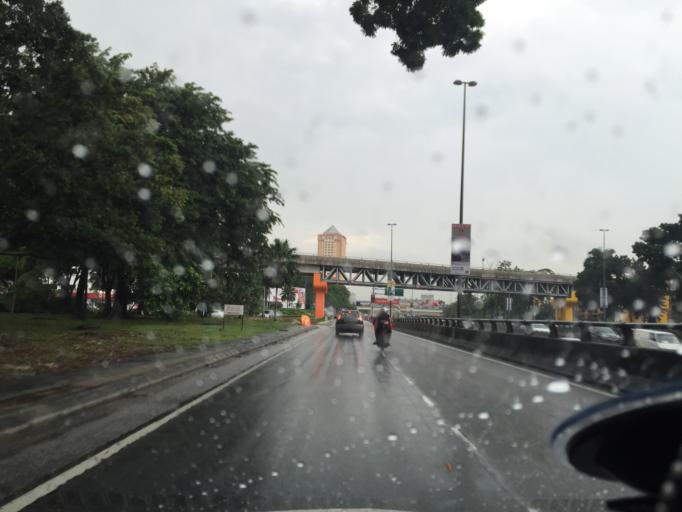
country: MY
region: Selangor
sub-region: Petaling
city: Petaling Jaya
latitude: 3.0742
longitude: 101.6116
